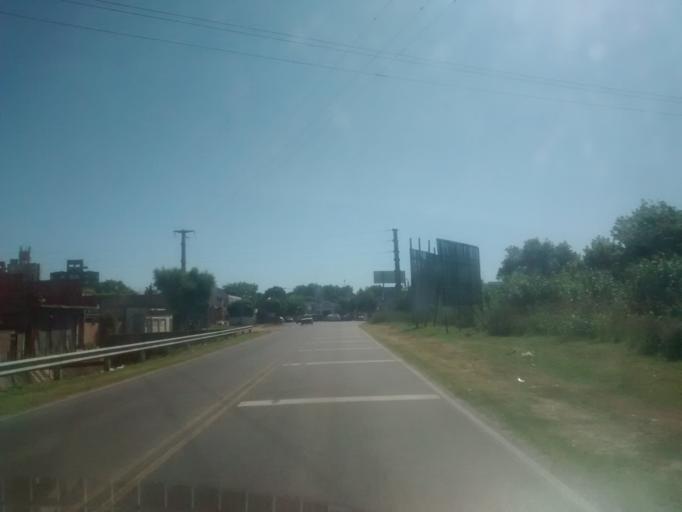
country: AR
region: Buenos Aires
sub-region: Partido de La Plata
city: La Plata
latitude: -34.9116
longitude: -57.9183
